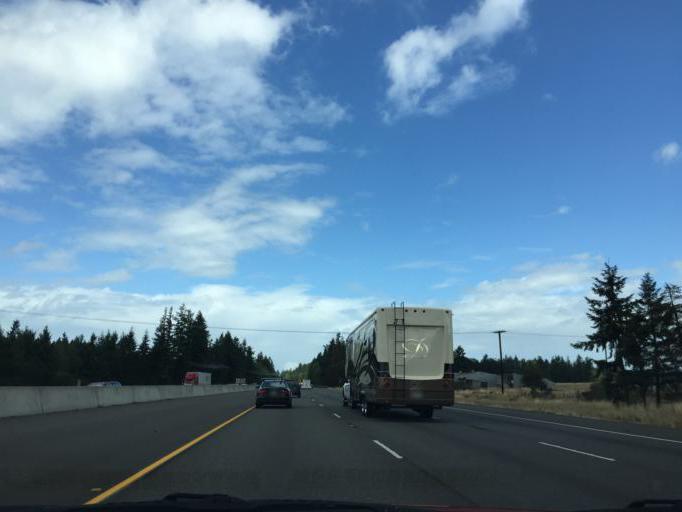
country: US
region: Washington
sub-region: Thurston County
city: Grand Mound
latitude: 46.8504
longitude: -122.9784
